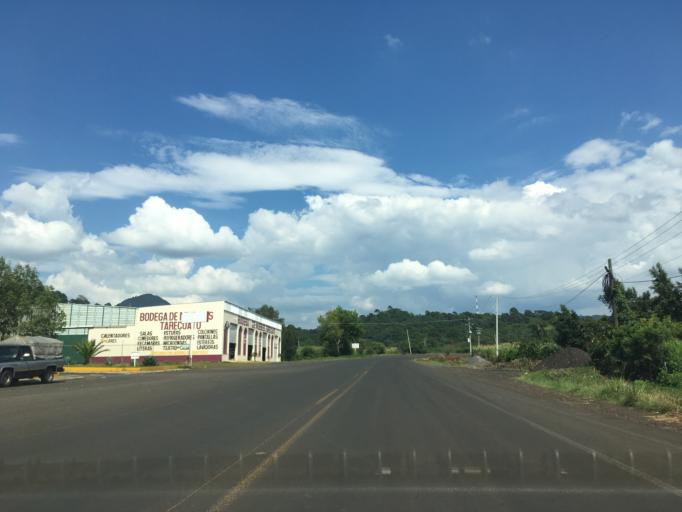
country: MX
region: Michoacan
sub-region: Tingueindin
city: Tingueindin
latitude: 19.8435
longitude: -102.4800
